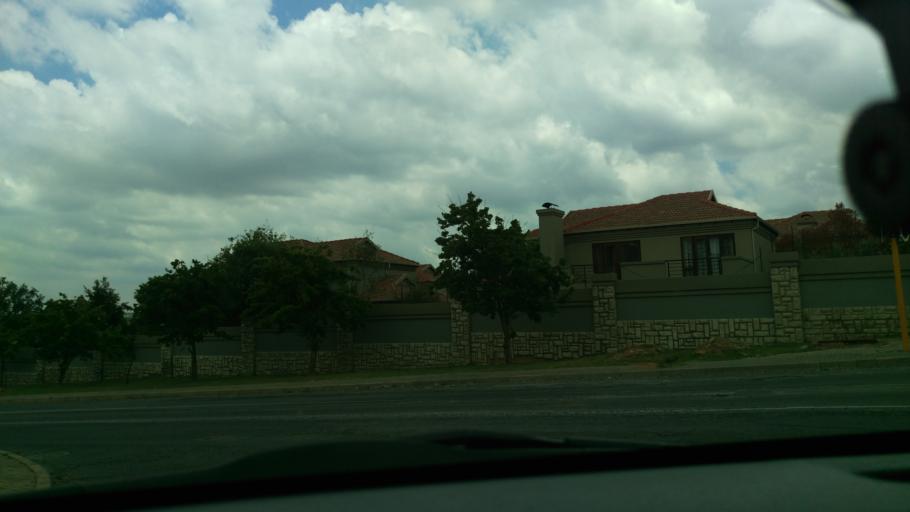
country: ZA
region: Gauteng
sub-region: City of Johannesburg Metropolitan Municipality
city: Midrand
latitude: -26.0412
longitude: 28.0449
